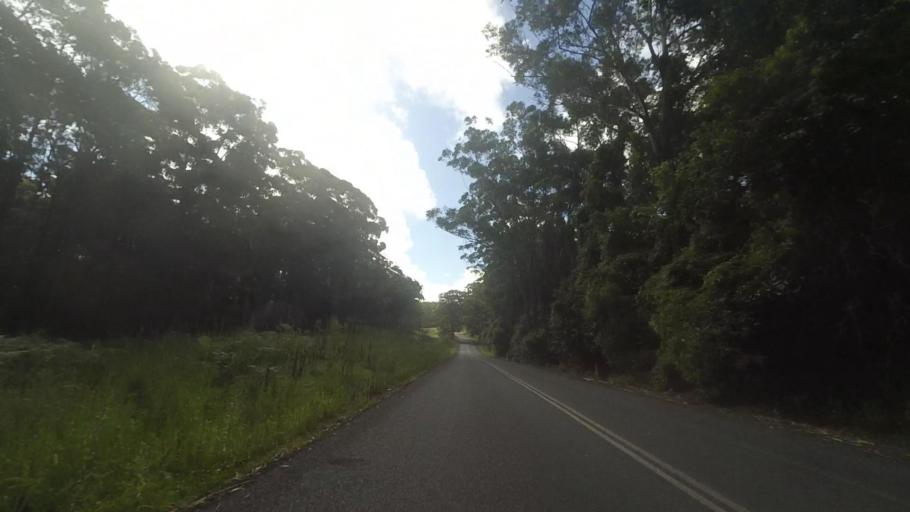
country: AU
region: New South Wales
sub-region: Great Lakes
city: Forster
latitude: -32.4311
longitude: 152.5125
